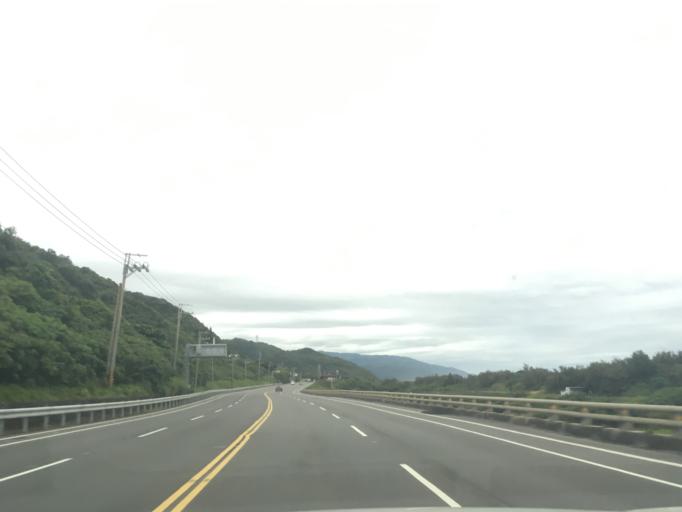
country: TW
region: Taiwan
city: Hengchun
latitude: 22.2978
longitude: 120.8888
